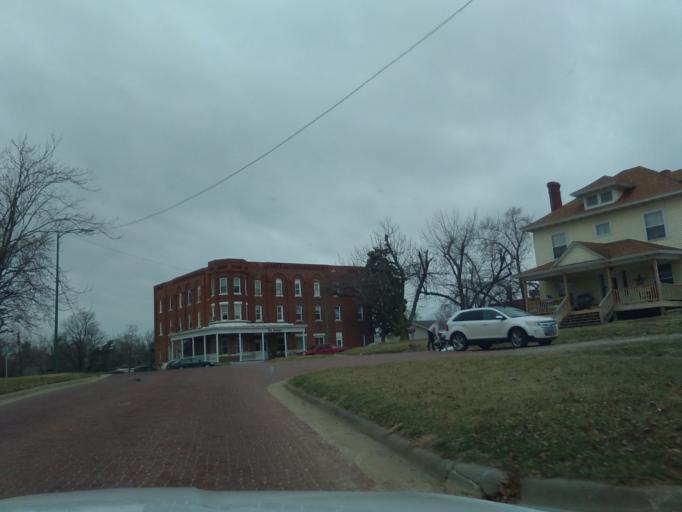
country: US
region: Nebraska
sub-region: Nemaha County
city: Auburn
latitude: 40.3860
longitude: -95.8426
